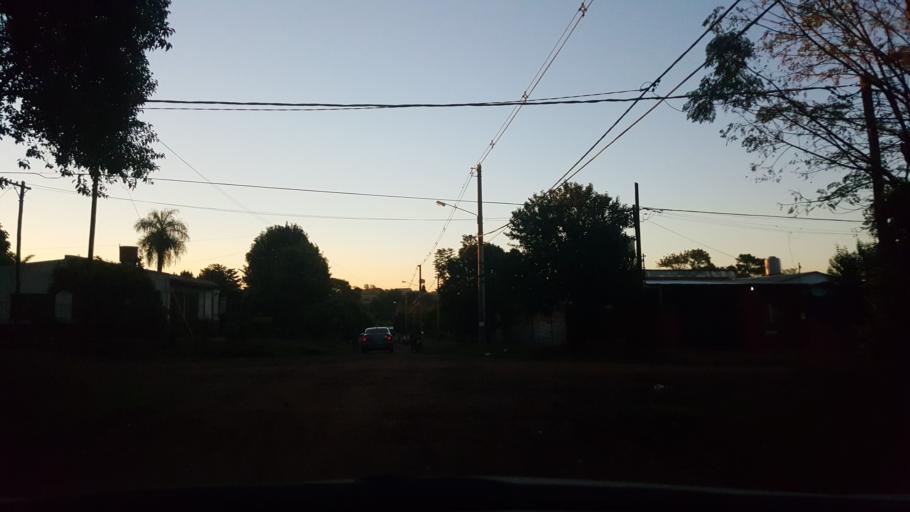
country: AR
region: Misiones
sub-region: Departamento de Capital
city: Posadas
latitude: -27.4228
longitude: -55.9014
